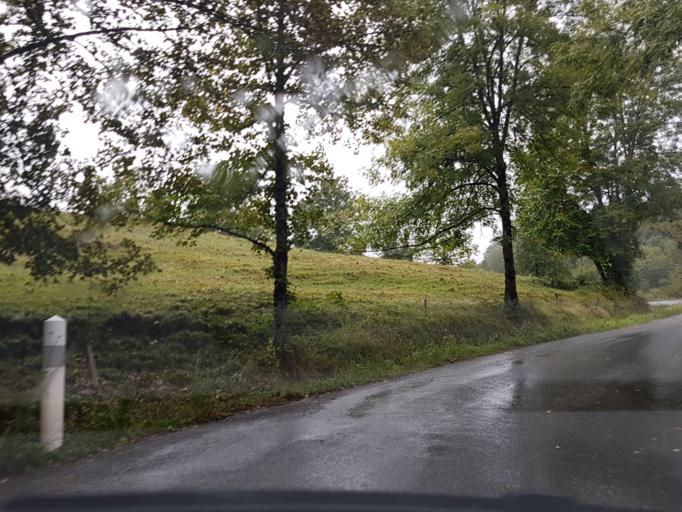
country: FR
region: Midi-Pyrenees
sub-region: Departement de l'Ariege
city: Montjoie-en-Couserans
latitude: 42.9021
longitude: 1.3629
